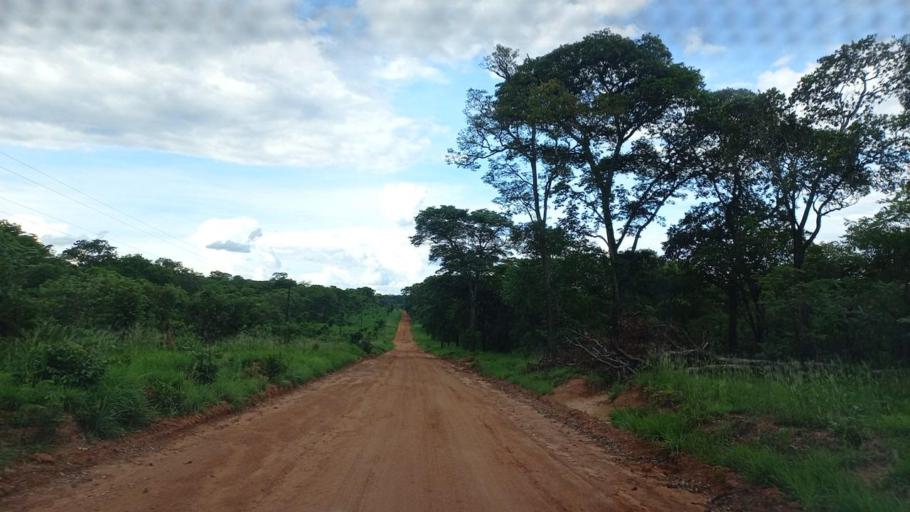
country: ZM
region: North-Western
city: Mwinilunga
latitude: -11.7900
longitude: 24.3727
